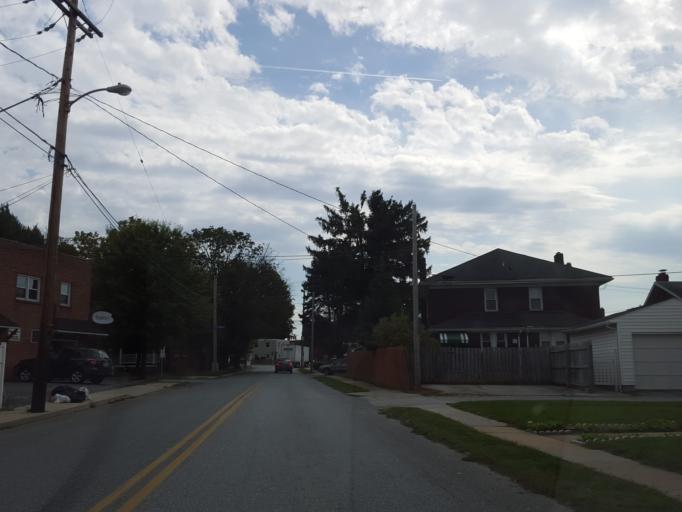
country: US
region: Pennsylvania
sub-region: York County
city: East York
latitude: 39.9688
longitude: -76.7008
